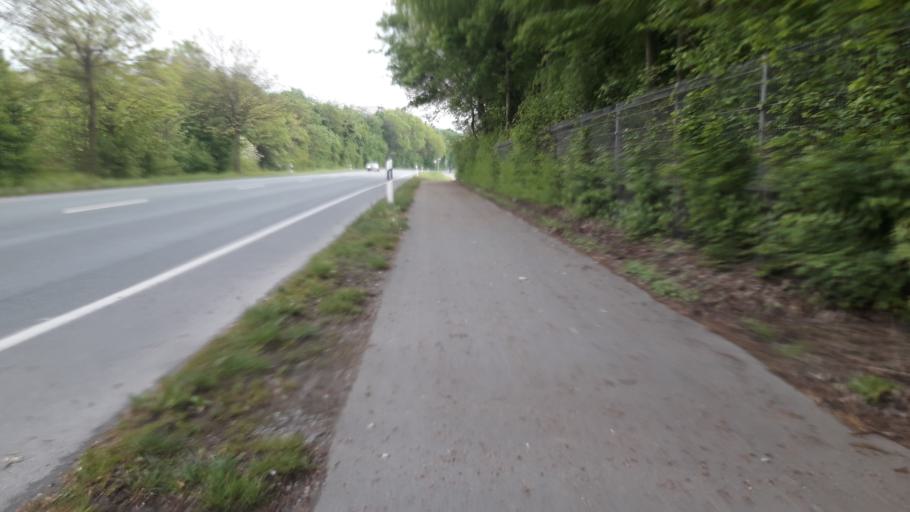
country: DE
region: North Rhine-Westphalia
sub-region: Regierungsbezirk Detmold
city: Paderborn
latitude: 51.6922
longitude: 8.7357
